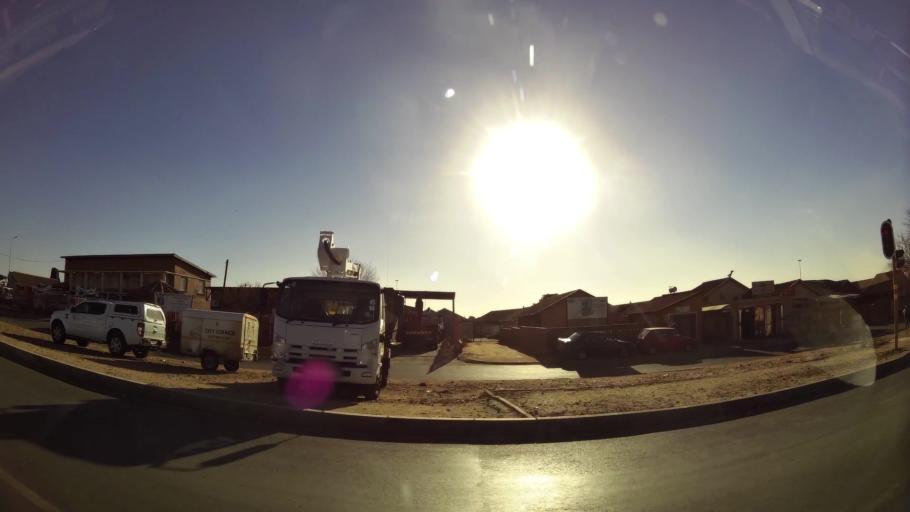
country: ZA
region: Gauteng
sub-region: Ekurhuleni Metropolitan Municipality
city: Tembisa
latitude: -26.0064
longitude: 28.2195
